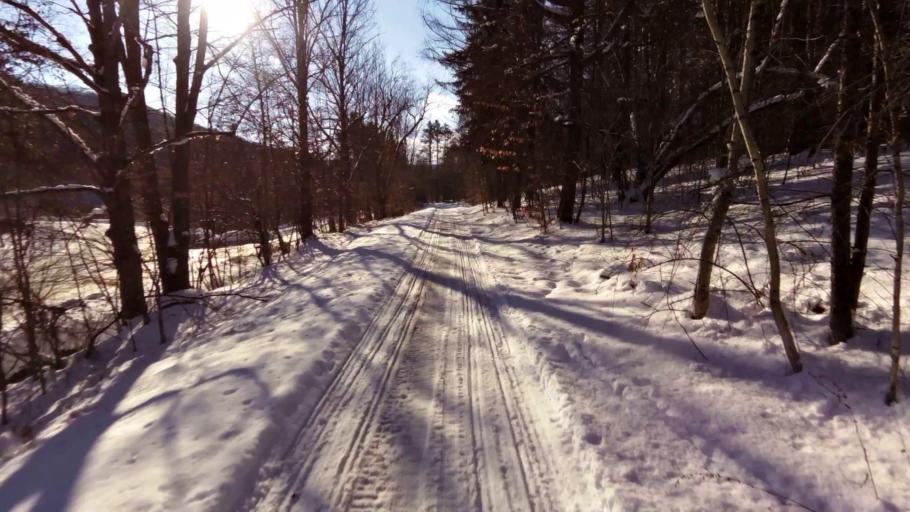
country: US
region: New York
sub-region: Cattaraugus County
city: Salamanca
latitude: 42.0983
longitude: -78.7488
